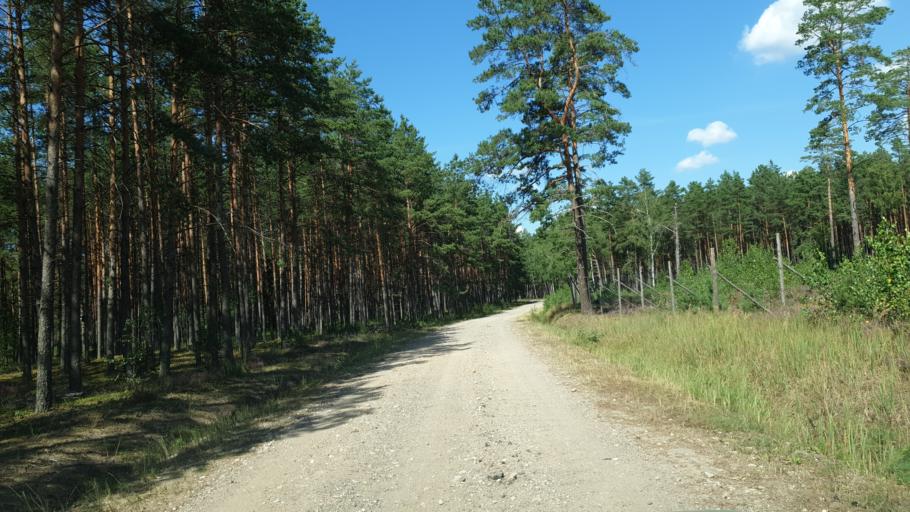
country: LT
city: Sirvintos
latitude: 54.9025
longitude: 24.9564
